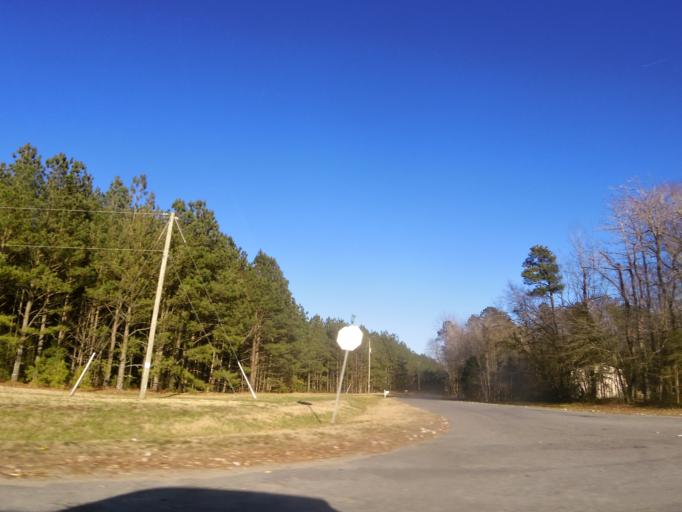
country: US
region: Virginia
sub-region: City of Franklin
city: Franklin
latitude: 36.6575
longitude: -76.8774
